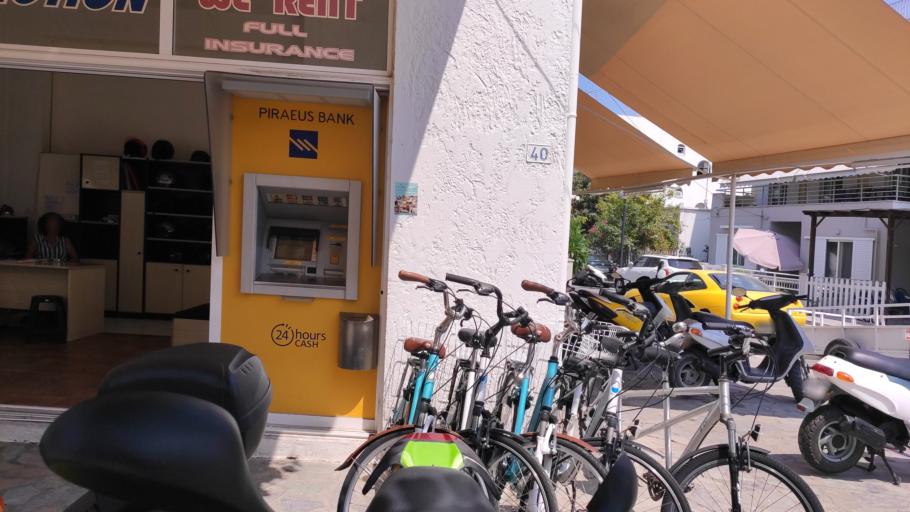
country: GR
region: South Aegean
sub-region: Nomos Dodekanisou
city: Kos
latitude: 36.8989
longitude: 27.2841
